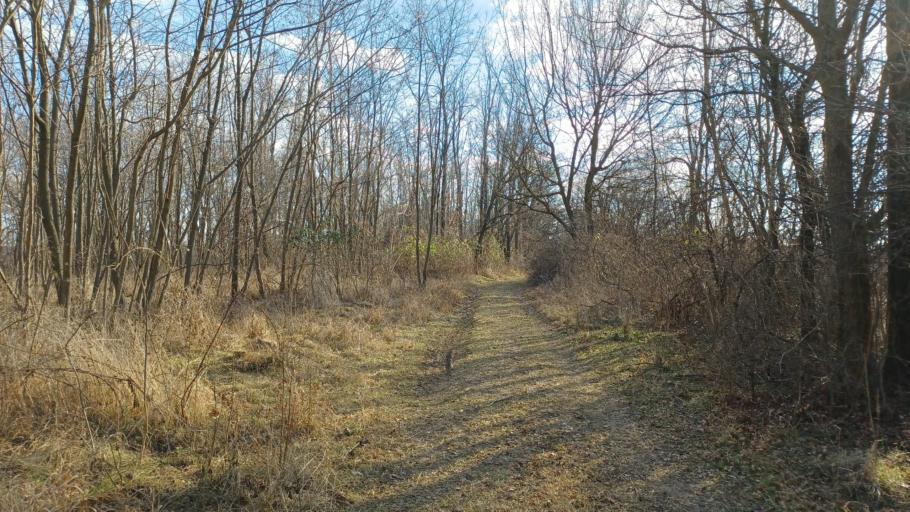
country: HU
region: Tolna
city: Szentgalpuszta
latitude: 46.3364
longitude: 18.6116
